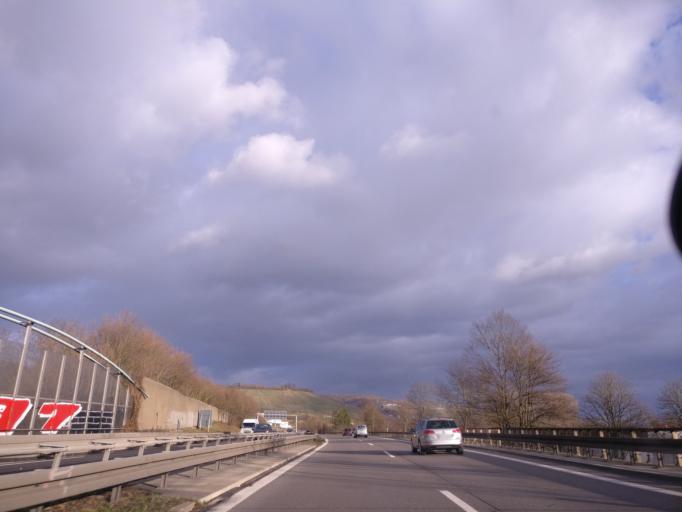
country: DE
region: Baden-Wuerttemberg
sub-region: Regierungsbezirk Stuttgart
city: Weinstadt-Endersbach
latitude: 48.8156
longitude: 9.3888
